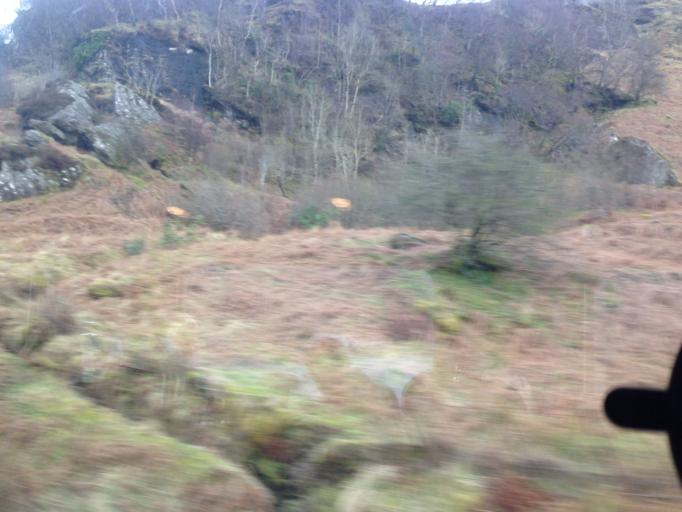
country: GB
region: Scotland
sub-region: Argyll and Bute
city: Garelochhead
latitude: 56.1783
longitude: -4.7731
